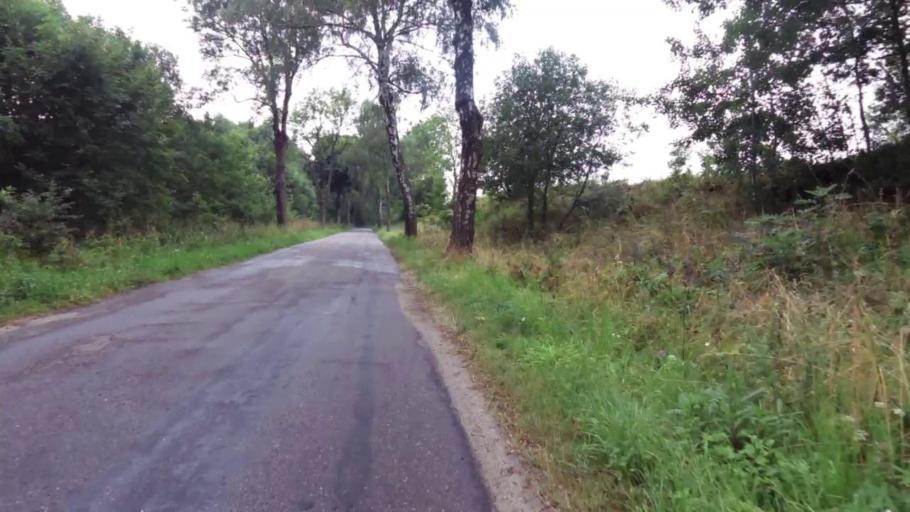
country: PL
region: West Pomeranian Voivodeship
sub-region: Powiat szczecinecki
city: Lubowo
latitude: 53.6057
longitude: 16.3402
